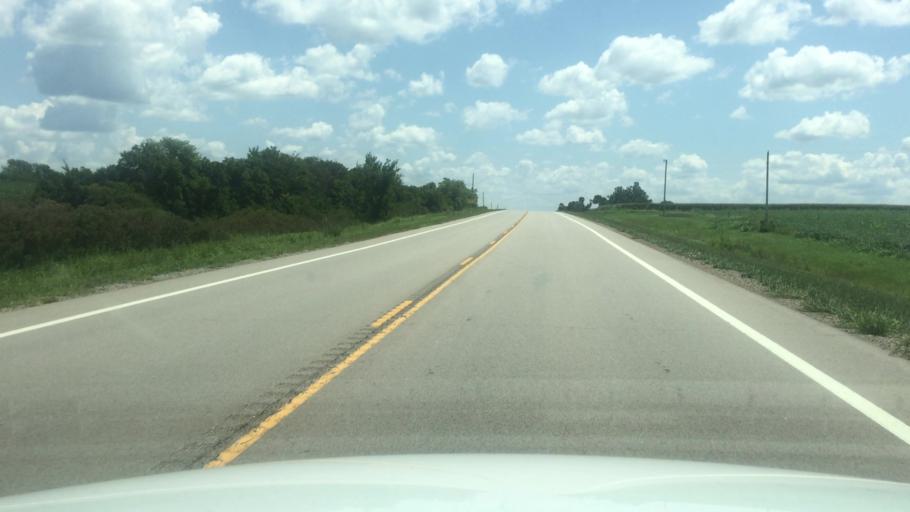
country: US
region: Kansas
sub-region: Brown County
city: Horton
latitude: 39.6109
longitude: -95.3450
